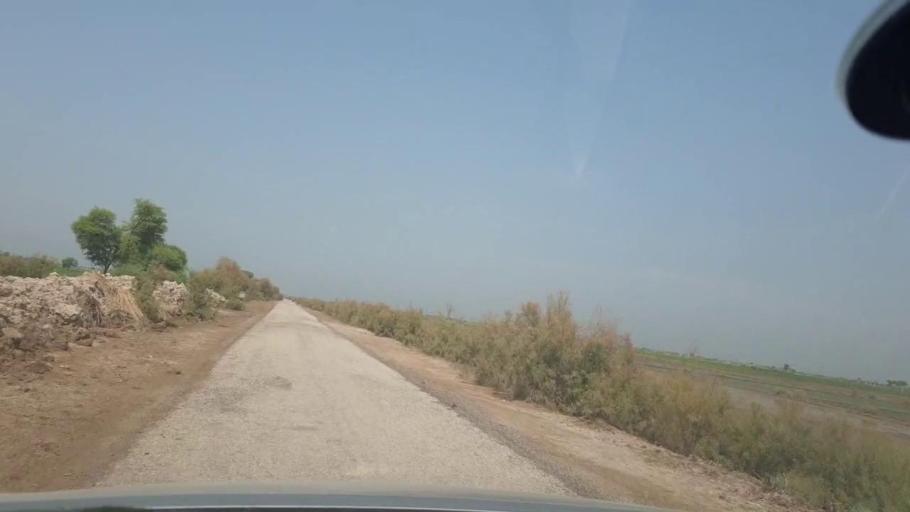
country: PK
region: Balochistan
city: Mehrabpur
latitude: 28.0590
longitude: 68.0725
